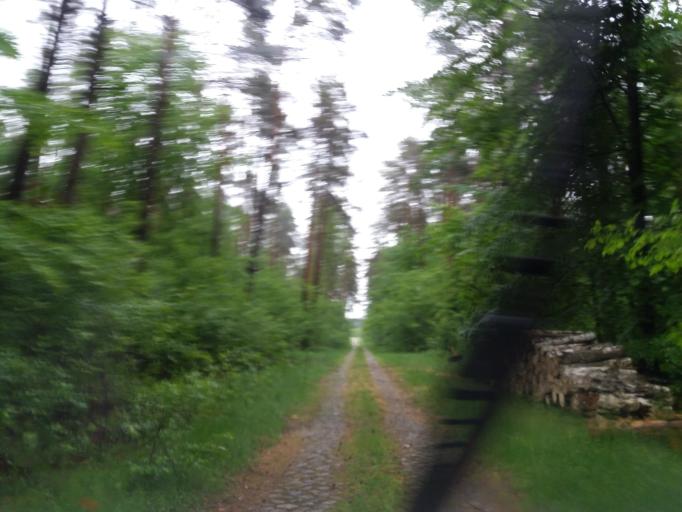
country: PL
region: Lubusz
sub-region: Powiat strzelecko-drezdenecki
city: Dobiegniew
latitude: 53.0198
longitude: 15.8630
